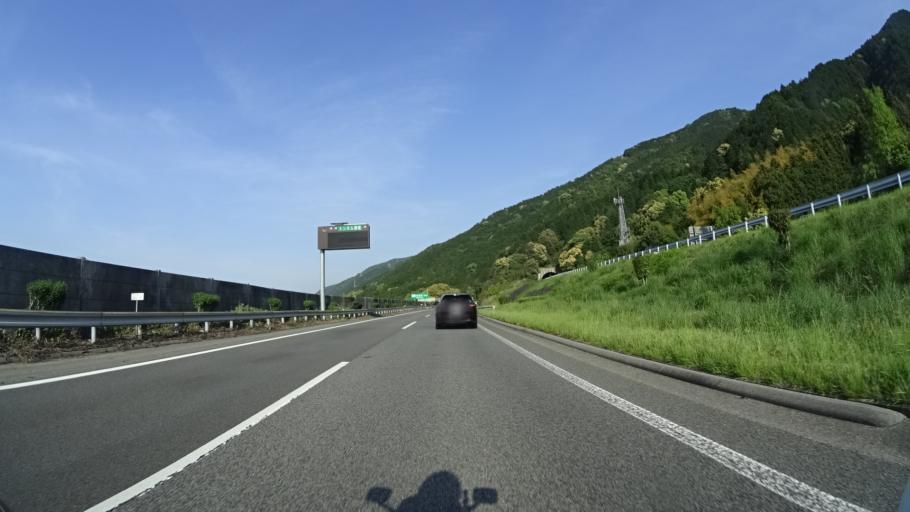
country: JP
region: Ehime
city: Niihama
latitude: 33.9176
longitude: 133.2932
